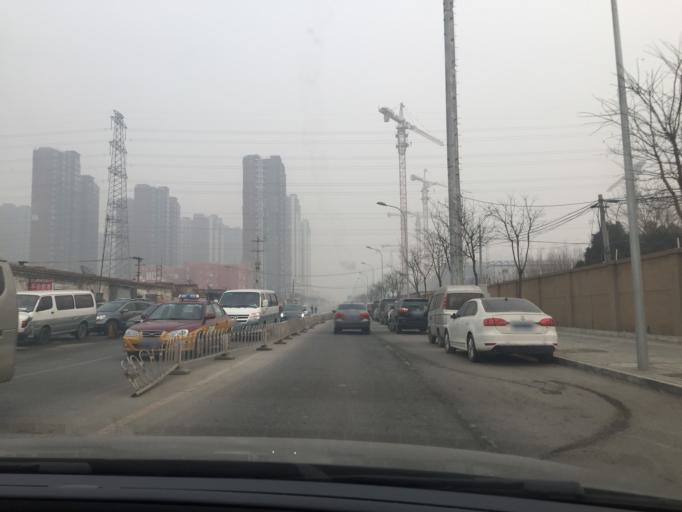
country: CN
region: Beijing
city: Qinghe
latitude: 40.0136
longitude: 116.3315
